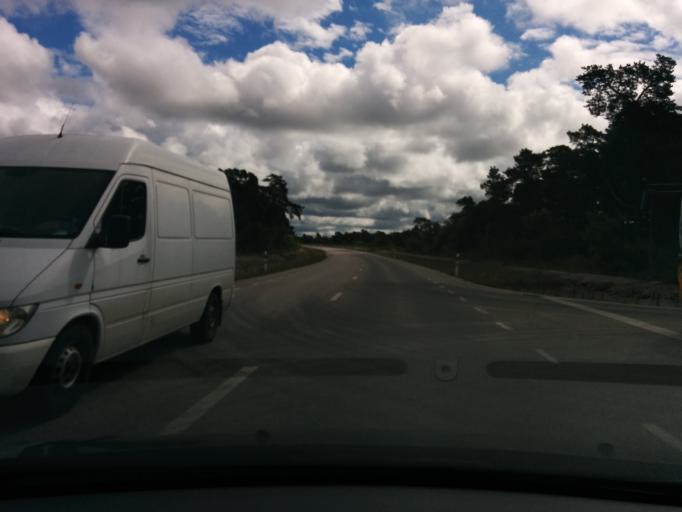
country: SE
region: Gotland
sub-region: Gotland
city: Visby
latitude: 57.6301
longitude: 18.3440
